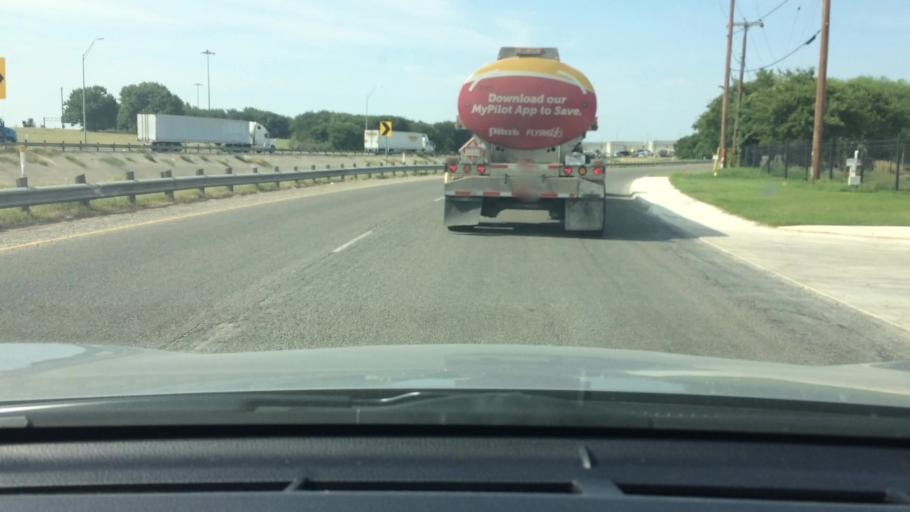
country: US
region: Texas
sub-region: Bexar County
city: Kirby
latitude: 29.4330
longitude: -98.3885
